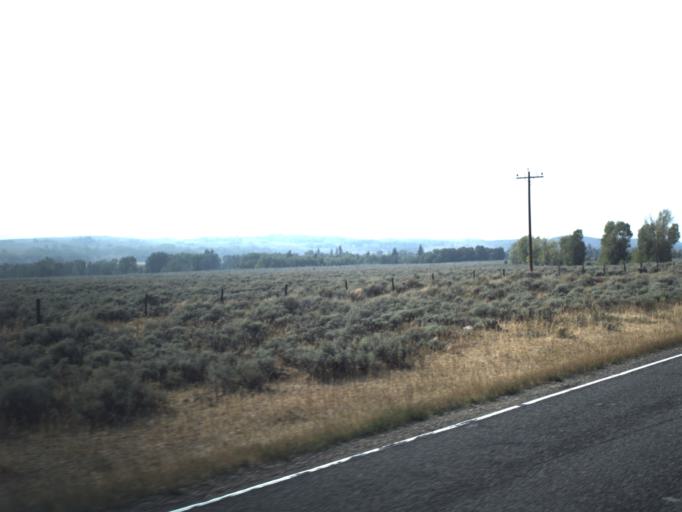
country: US
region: Wyoming
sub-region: Uinta County
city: Evanston
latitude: 40.9736
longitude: -110.8511
